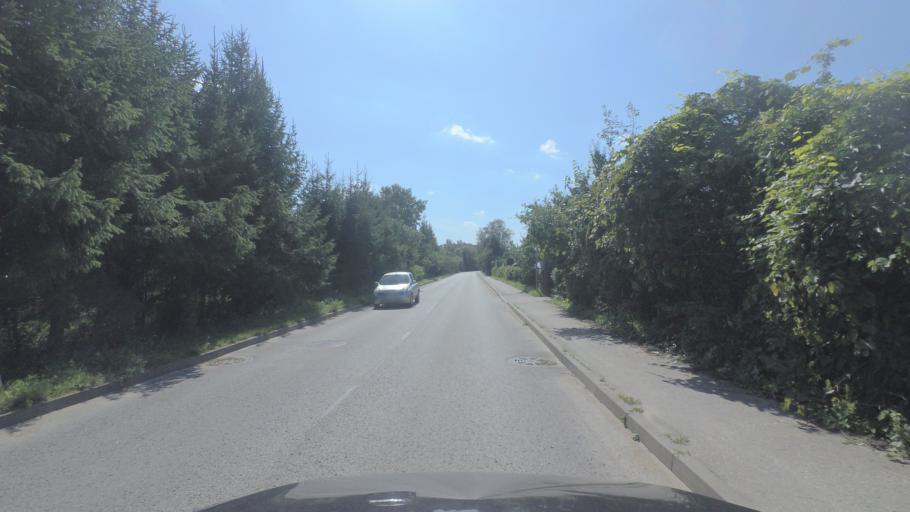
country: LT
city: Nemencine
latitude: 54.8343
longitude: 25.3691
